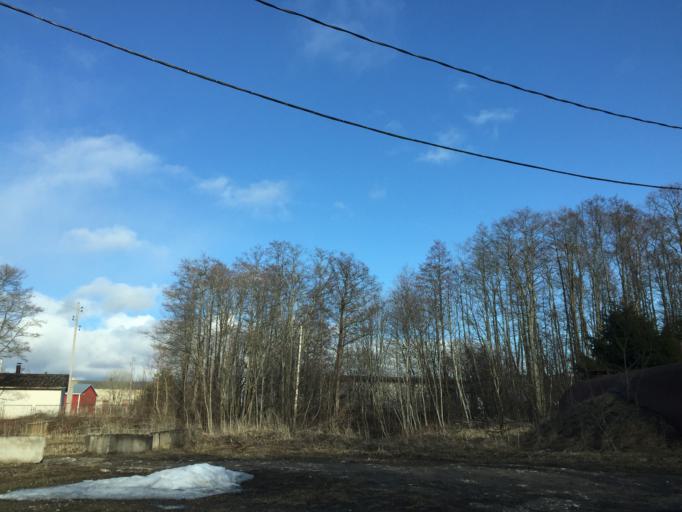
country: EE
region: Laeaene
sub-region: Haapsalu linn
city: Haapsalu
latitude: 58.9325
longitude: 23.5330
